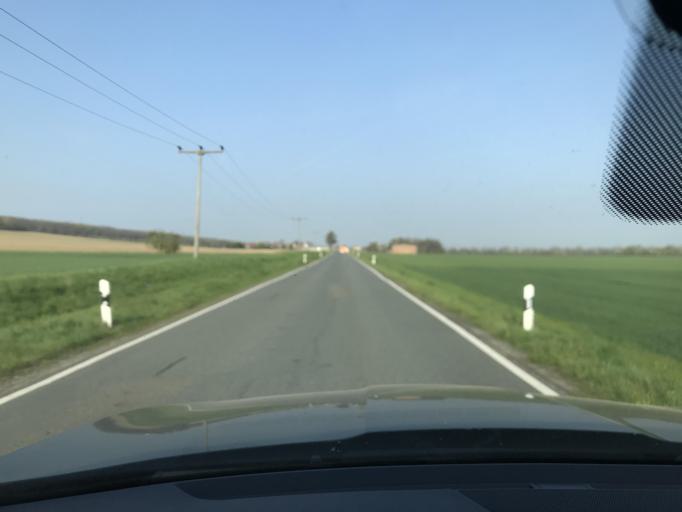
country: DE
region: Saxony-Anhalt
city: Schwanebeck
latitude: 51.9827
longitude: 11.0980
